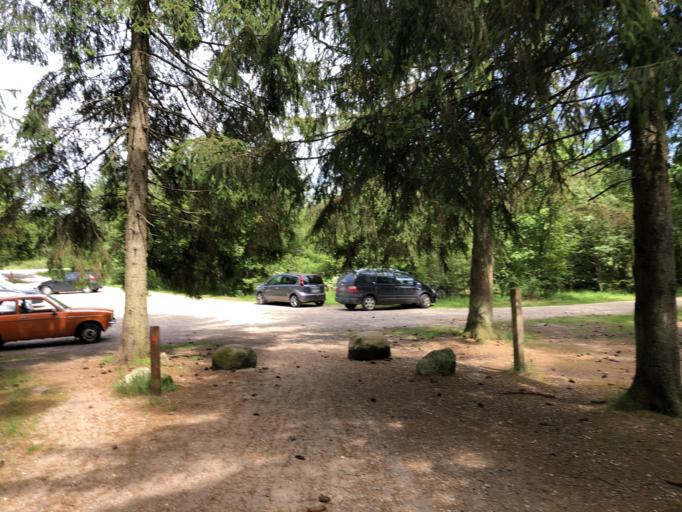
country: DK
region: Central Jutland
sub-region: Holstebro Kommune
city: Holstebro
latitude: 56.3494
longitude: 8.5859
